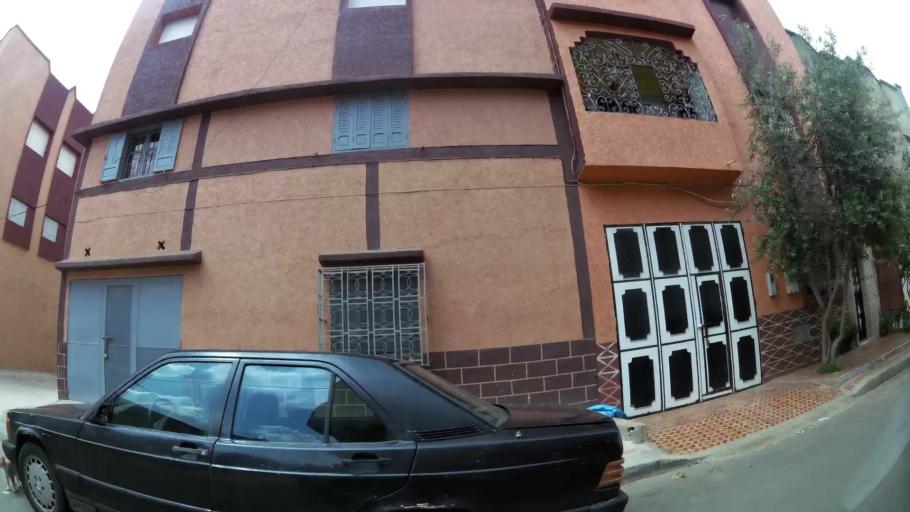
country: MA
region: Rabat-Sale-Zemmour-Zaer
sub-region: Khemisset
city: Tiflet
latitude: 33.8910
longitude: -6.3326
